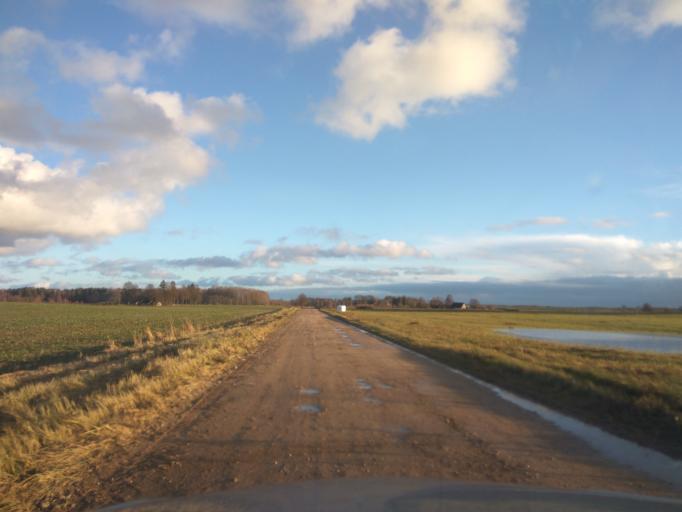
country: LV
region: Aizpute
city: Aizpute
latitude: 56.7742
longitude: 21.6944
